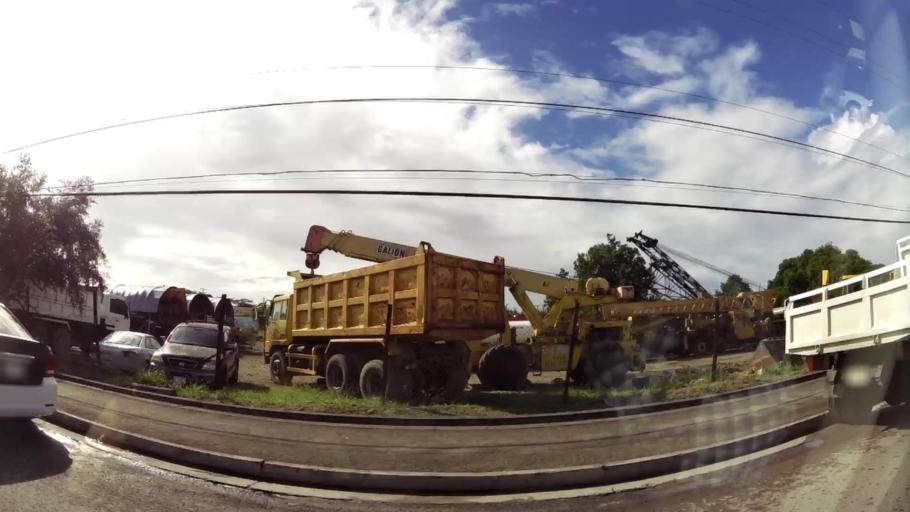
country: AG
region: Saint John
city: Saint John's
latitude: 17.1170
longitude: -61.8284
